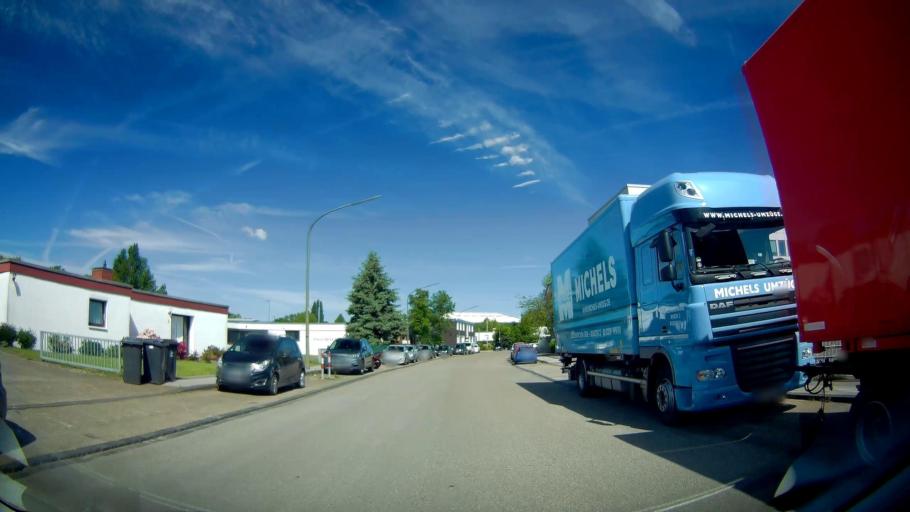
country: DE
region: North Rhine-Westphalia
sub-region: Regierungsbezirk Munster
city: Gelsenkirchen
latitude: 51.5457
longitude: 7.0746
